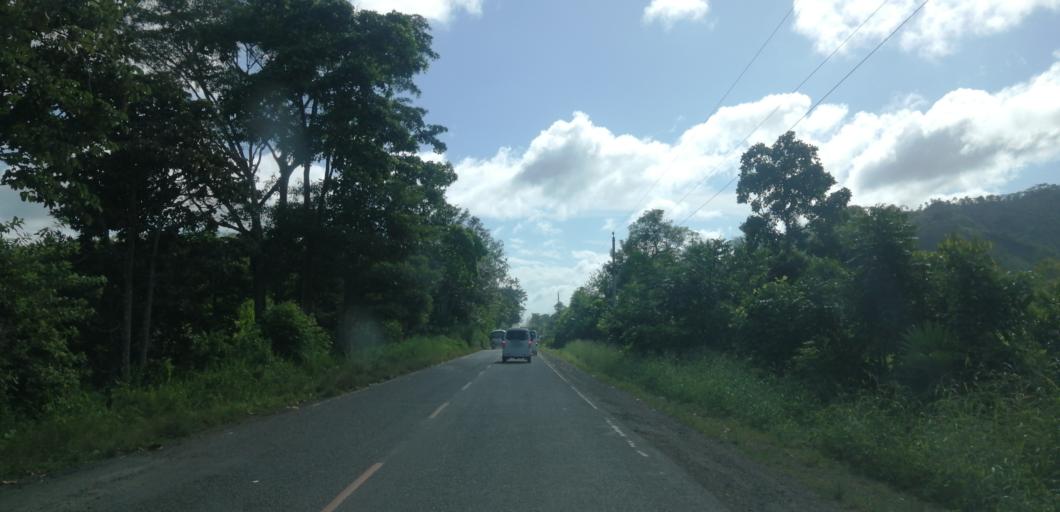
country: PA
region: Panama
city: Union Santena
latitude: 9.0498
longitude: -78.6383
